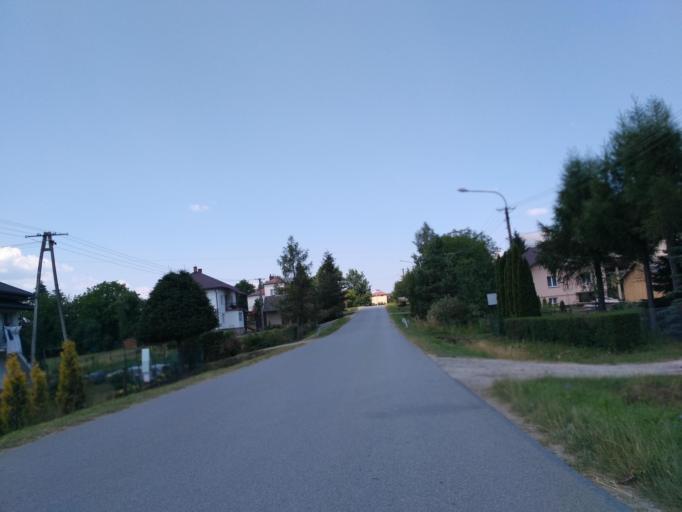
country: PL
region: Subcarpathian Voivodeship
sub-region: Powiat sanocki
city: Niebieszczany
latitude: 49.5149
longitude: 22.1405
